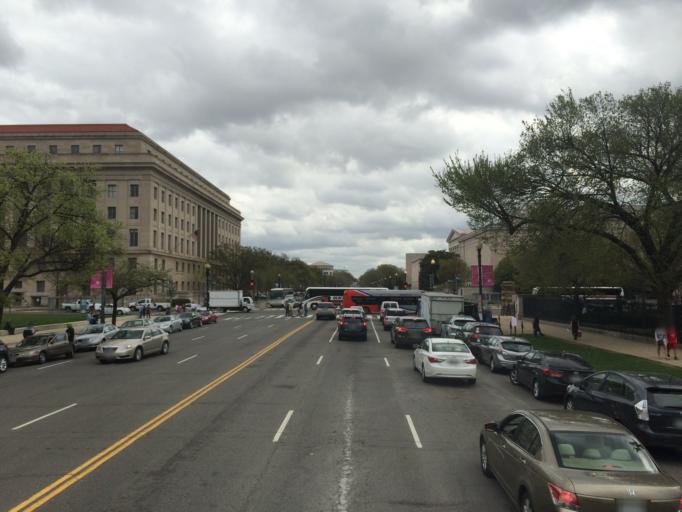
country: US
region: Washington, D.C.
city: Washington, D.C.
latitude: 38.8921
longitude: -77.0229
